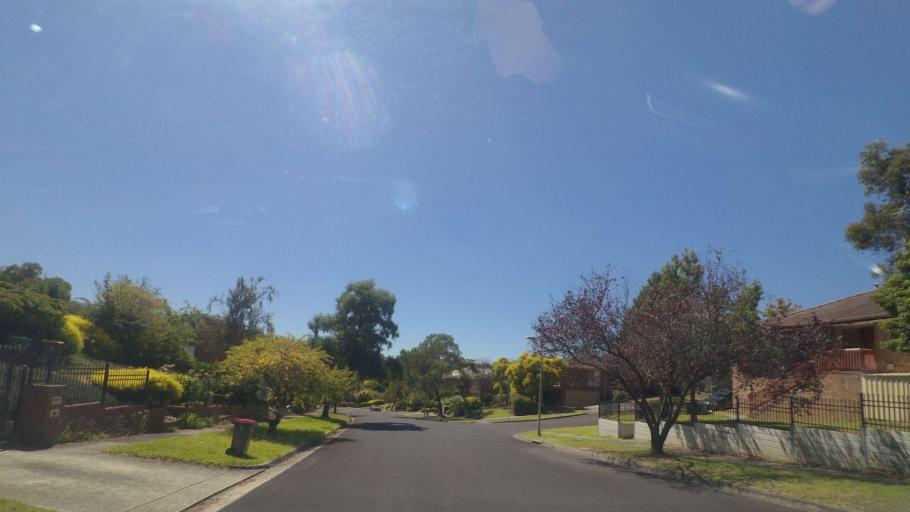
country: AU
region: Victoria
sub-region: Manningham
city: Donvale
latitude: -37.7699
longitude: 145.1769
